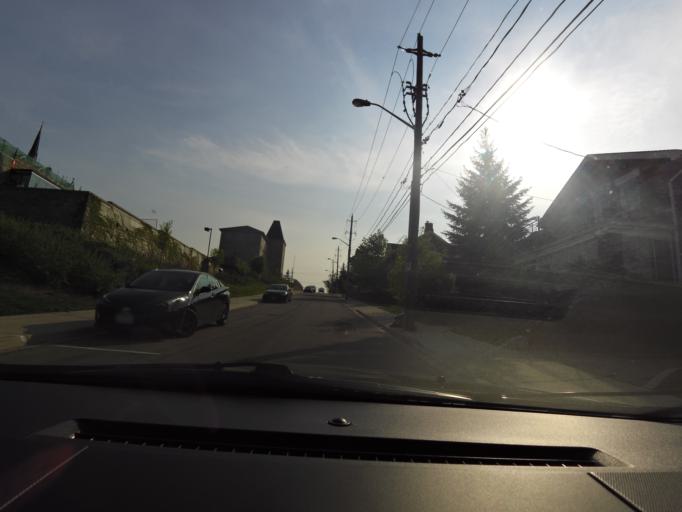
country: CA
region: Ontario
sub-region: Wellington County
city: Guelph
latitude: 43.5441
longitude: -80.2513
